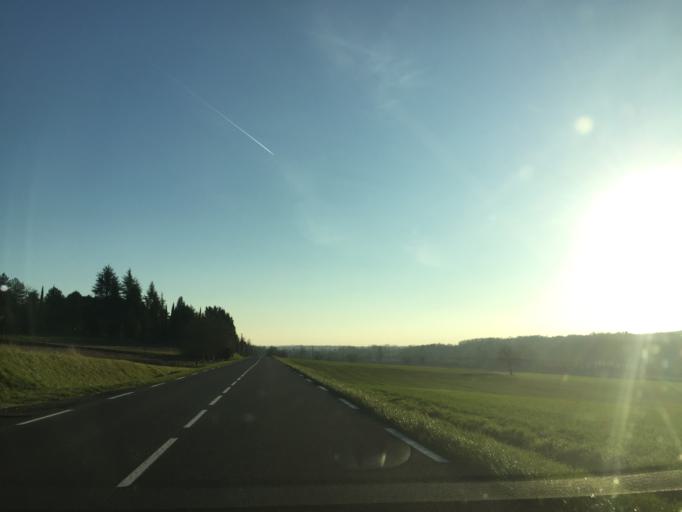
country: FR
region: Poitou-Charentes
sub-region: Departement de la Charente
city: Chalais
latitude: 45.2431
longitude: 0.0382
